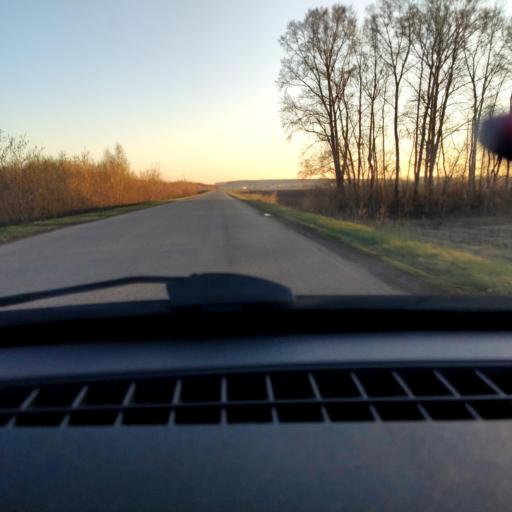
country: RU
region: Bashkortostan
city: Avdon
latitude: 54.5369
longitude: 55.6441
